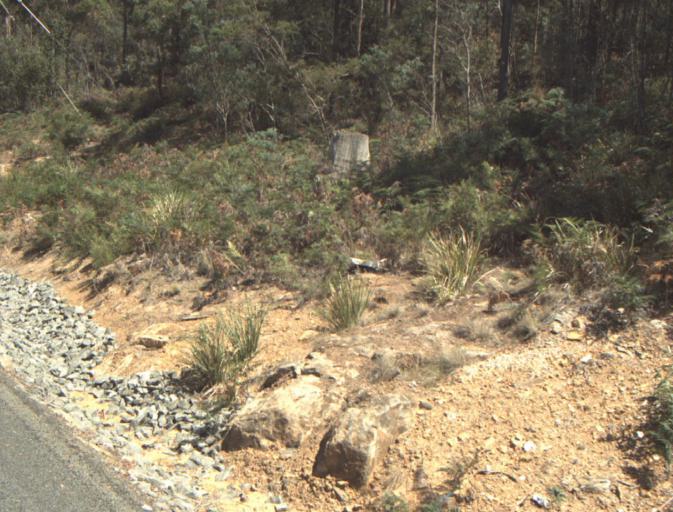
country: AU
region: Tasmania
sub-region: Launceston
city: Mayfield
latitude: -41.3203
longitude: 147.1226
